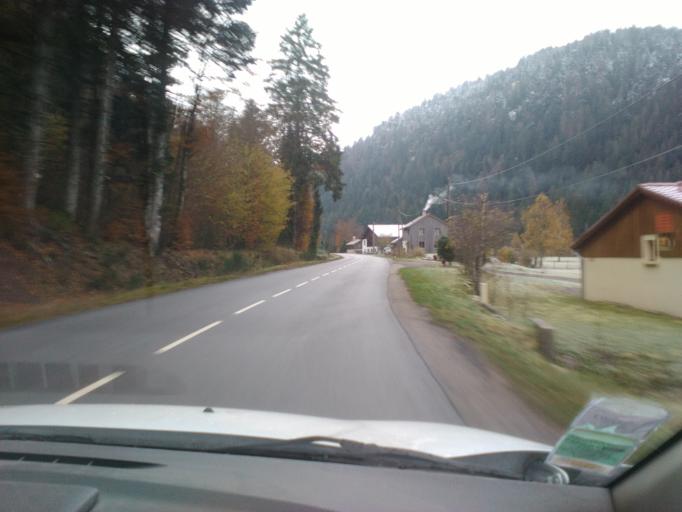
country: FR
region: Lorraine
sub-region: Departement des Vosges
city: Xonrupt-Longemer
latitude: 48.0653
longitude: 6.9610
